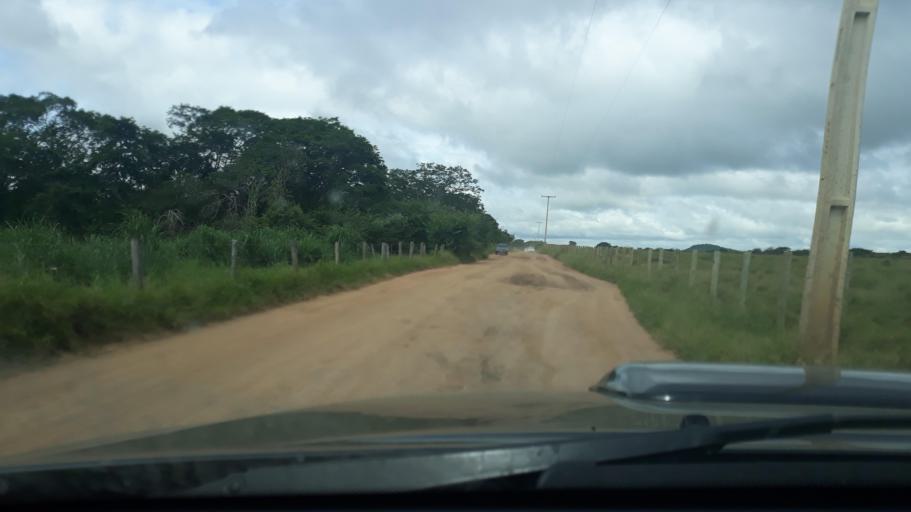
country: BR
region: Bahia
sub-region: Riacho De Santana
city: Riacho de Santana
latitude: -13.9011
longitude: -42.8907
